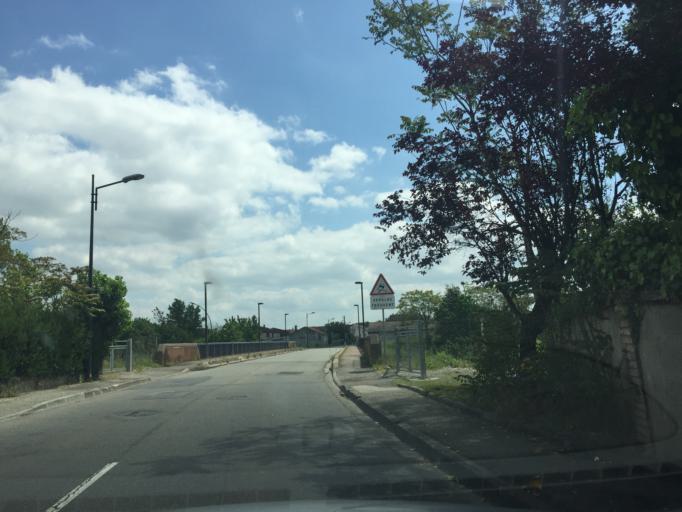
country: FR
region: Midi-Pyrenees
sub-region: Departement de la Haute-Garonne
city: Aucamville
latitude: 43.6475
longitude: 1.4434
